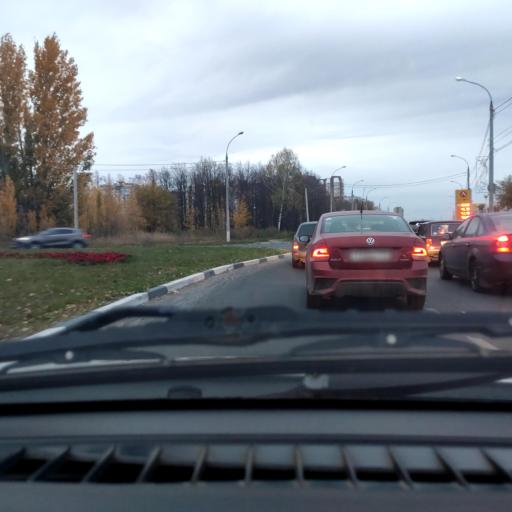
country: RU
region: Samara
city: Tol'yatti
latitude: 53.4956
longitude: 49.2893
